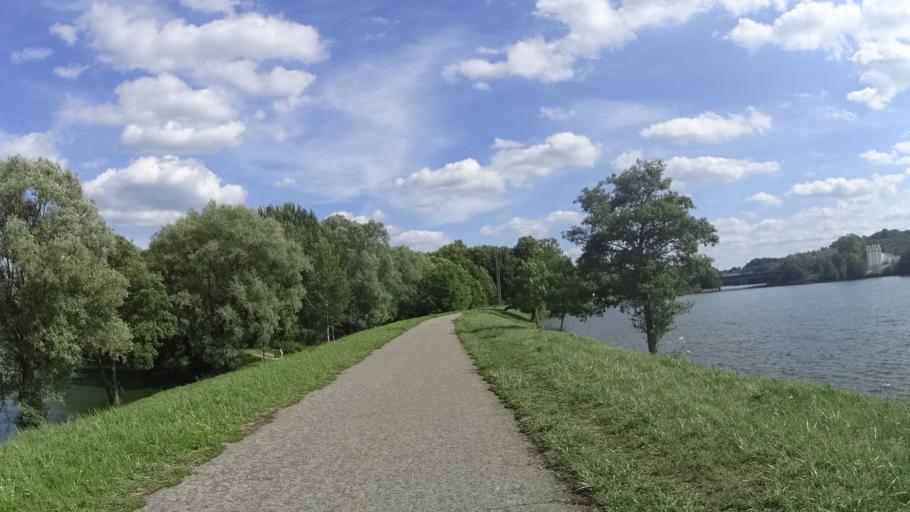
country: FR
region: Lorraine
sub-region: Departement de Meurthe-et-Moselle
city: Dommartin-les-Toul
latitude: 48.6605
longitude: 5.8960
